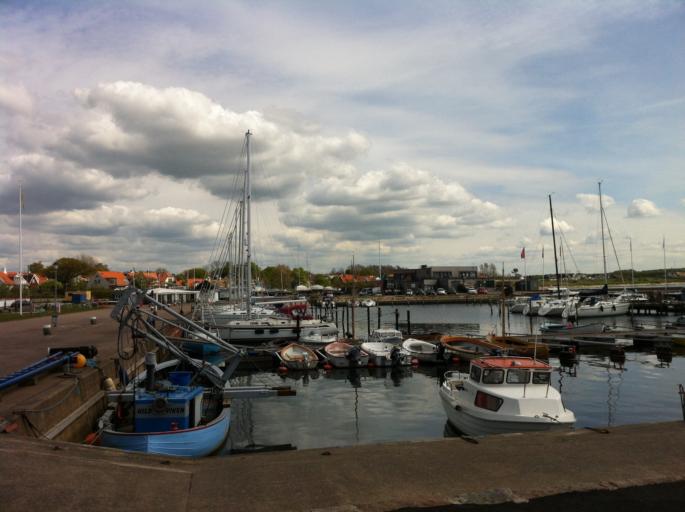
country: SE
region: Skane
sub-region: Hoganas Kommun
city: Hoganas
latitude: 56.1428
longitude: 12.5772
